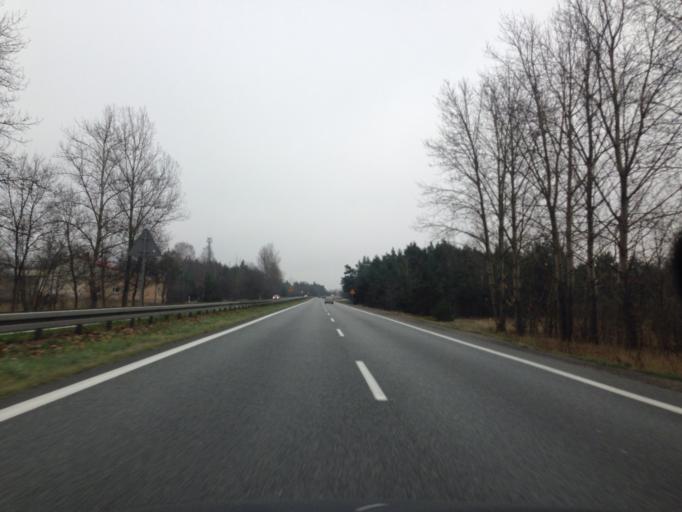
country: PL
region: Silesian Voivodeship
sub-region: Powiat bedzinski
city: Siewierz
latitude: 50.4830
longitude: 19.2207
